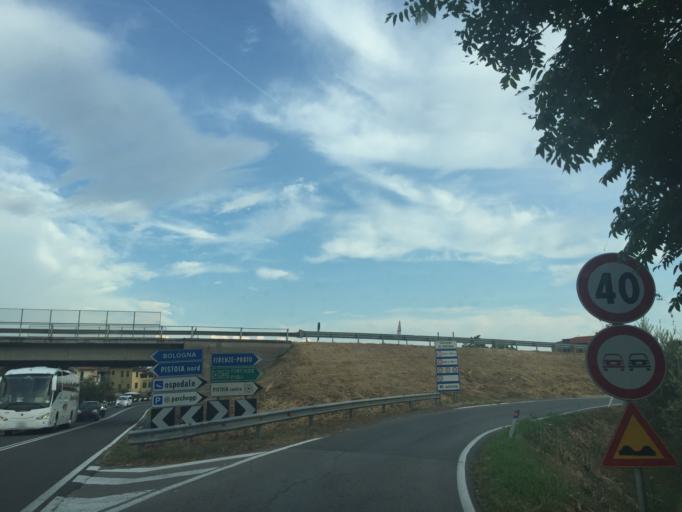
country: IT
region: Tuscany
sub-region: Provincia di Pistoia
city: Pistoia
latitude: 43.9567
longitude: 10.8980
